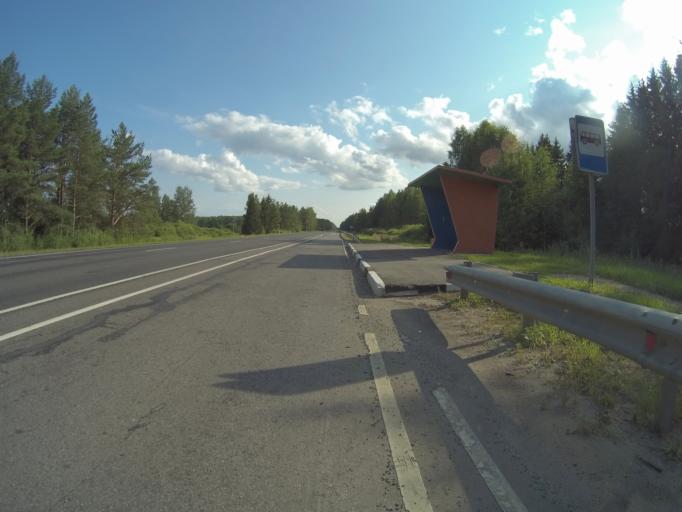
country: RU
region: Ivanovo
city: Novoye Leushino
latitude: 56.6394
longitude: 40.5763
